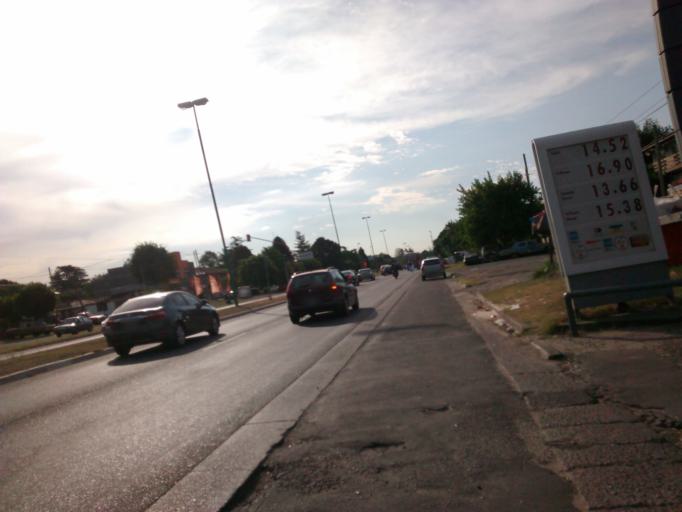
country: AR
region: Buenos Aires
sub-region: Partido de La Plata
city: La Plata
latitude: -34.8510
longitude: -58.0887
